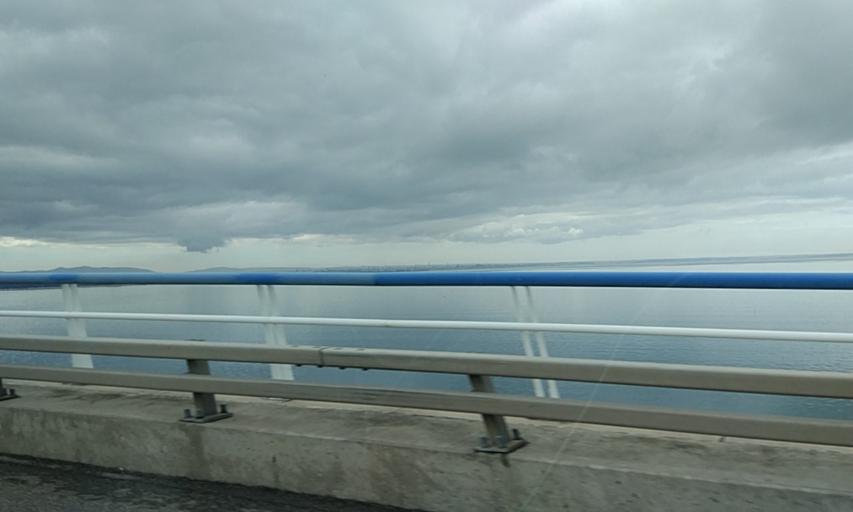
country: PT
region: Lisbon
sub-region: Loures
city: Moscavide
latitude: 38.7576
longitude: -9.0374
